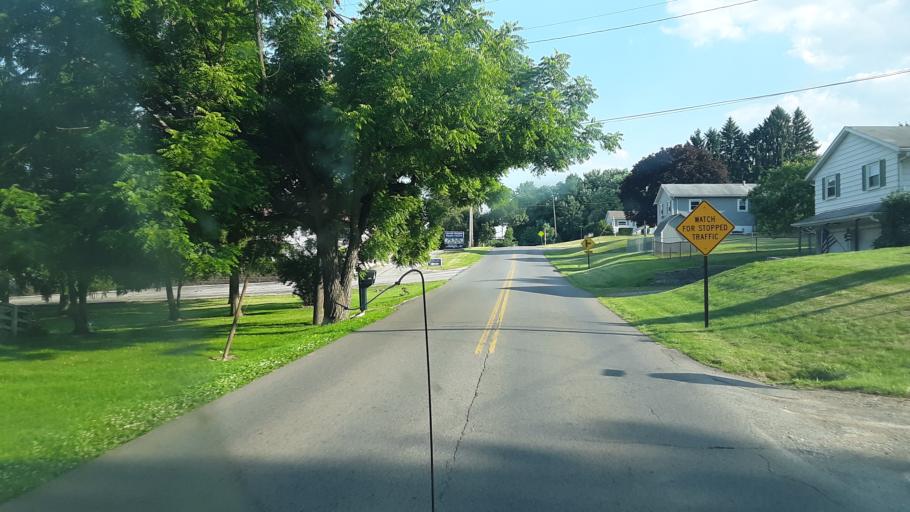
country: US
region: Ohio
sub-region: Richland County
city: Lincoln Heights
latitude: 40.7729
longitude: -82.4748
